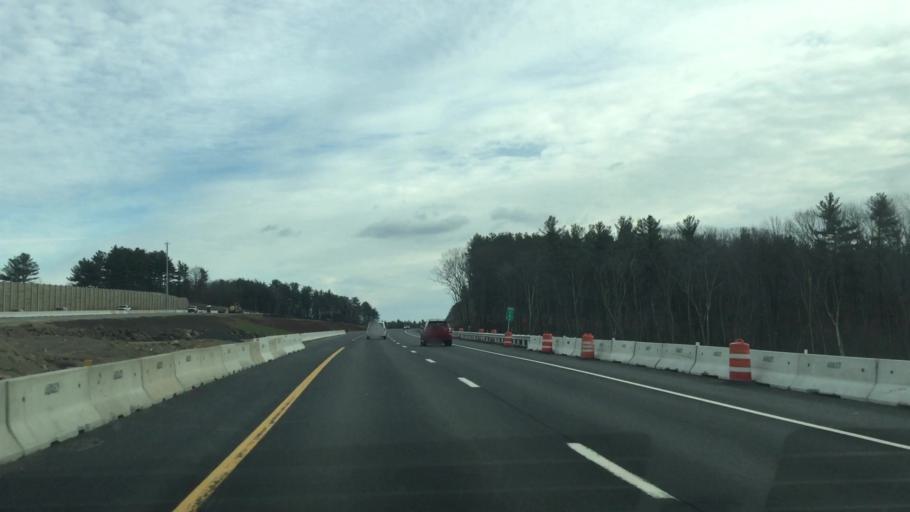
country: US
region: New Hampshire
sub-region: Rockingham County
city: Derry
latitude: 42.8588
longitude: -71.3283
